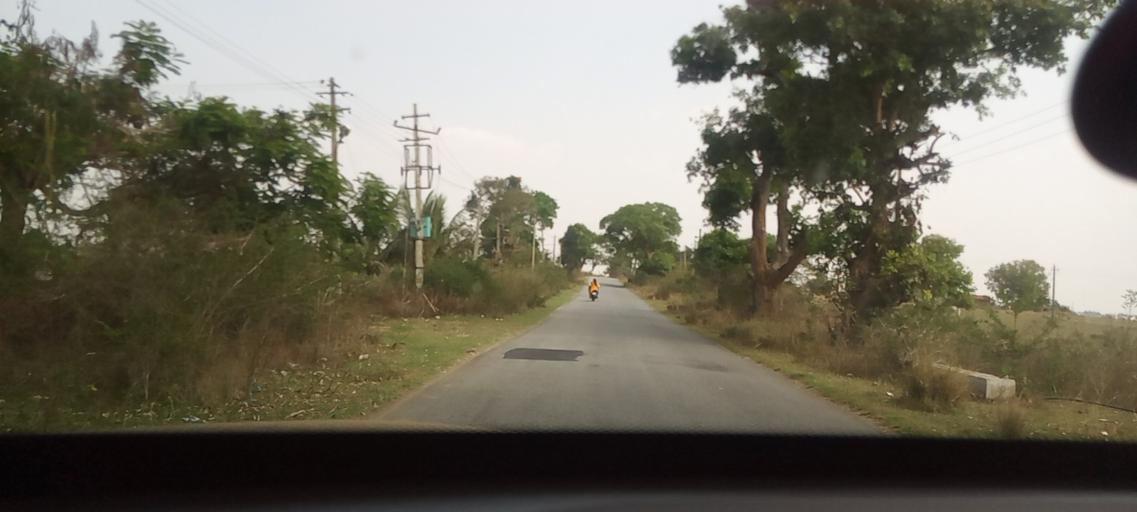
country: IN
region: Karnataka
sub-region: Hassan
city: Belur
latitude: 13.1789
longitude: 75.8454
